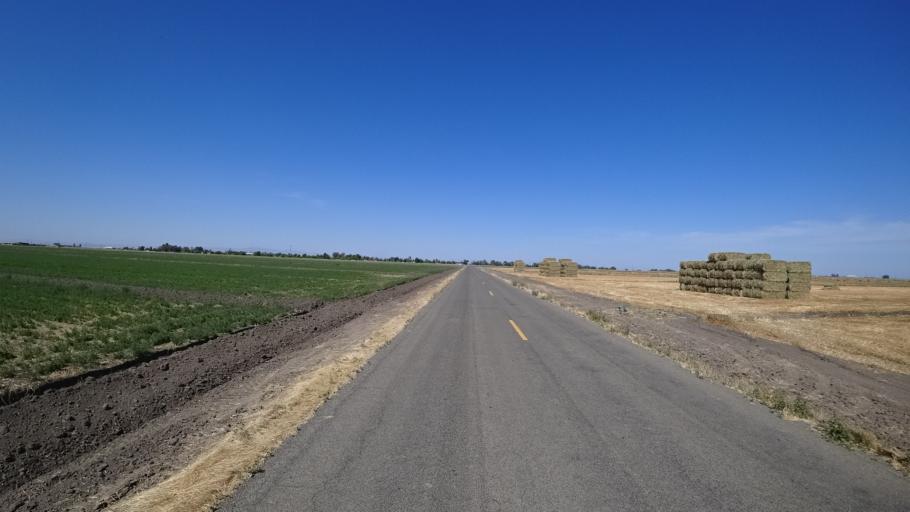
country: US
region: California
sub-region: Kings County
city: Stratford
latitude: 36.1967
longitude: -119.8087
